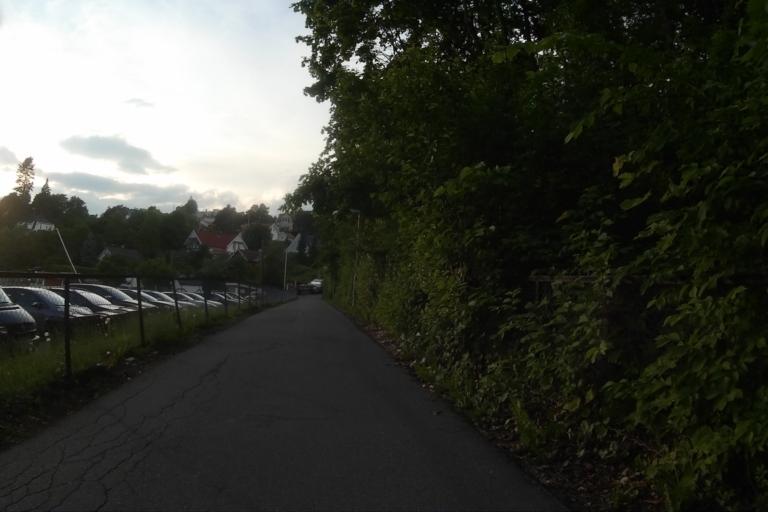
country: NO
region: Oslo
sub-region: Oslo
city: Oslo
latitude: 59.8770
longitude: 10.7757
